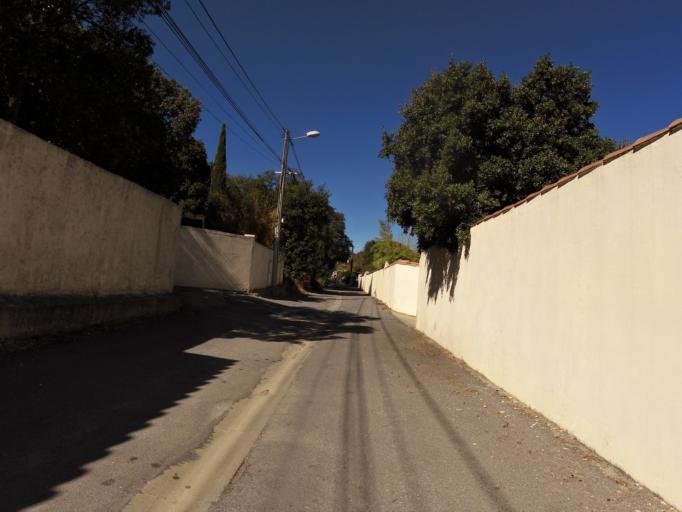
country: FR
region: Languedoc-Roussillon
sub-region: Departement du Gard
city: Nages-et-Solorgues
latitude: 43.7695
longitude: 4.2396
